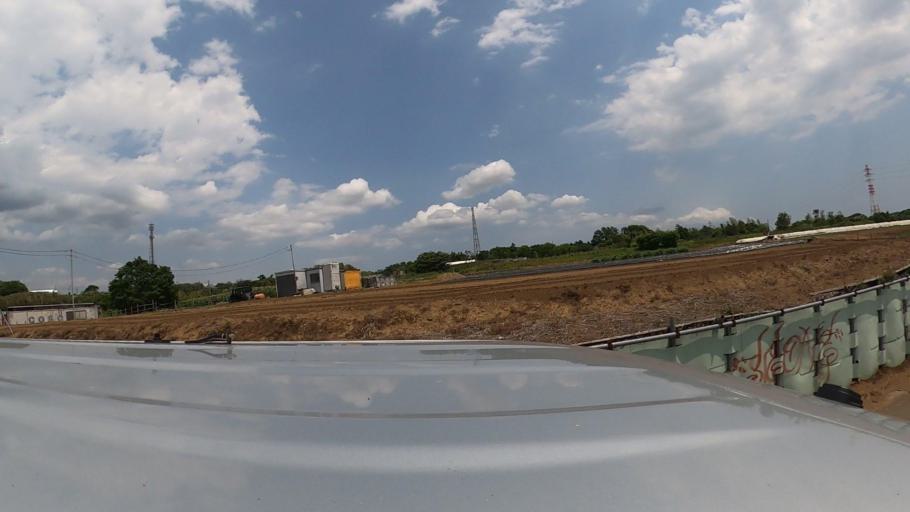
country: JP
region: Kanagawa
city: Chigasaki
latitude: 35.3869
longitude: 139.4187
